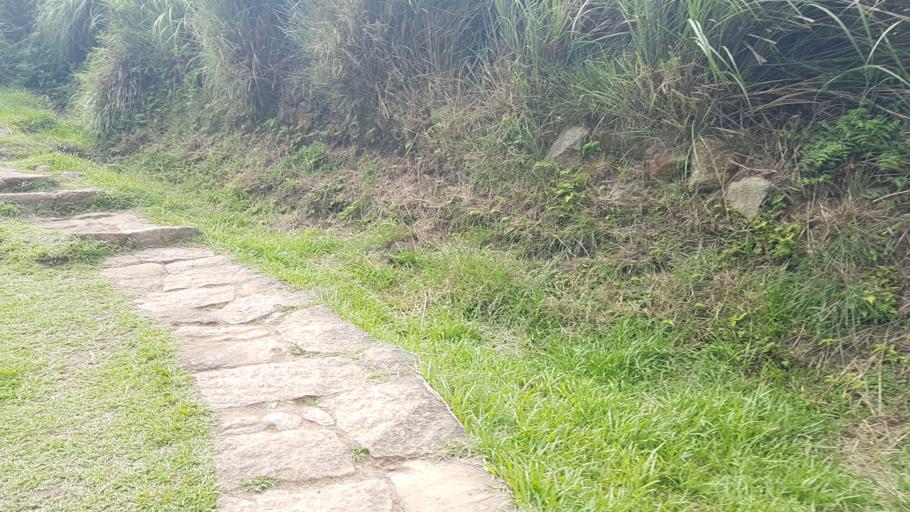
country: TW
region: Taipei
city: Taipei
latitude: 25.1661
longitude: 121.5785
